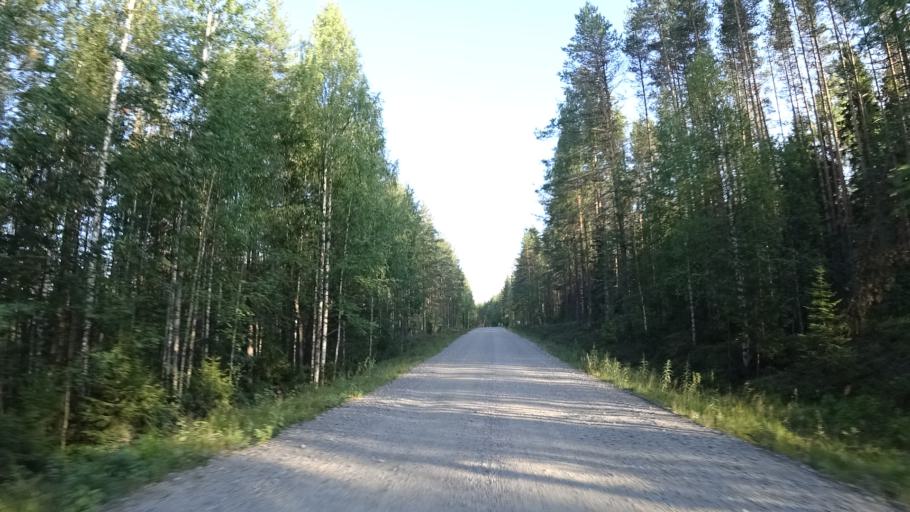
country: FI
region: North Karelia
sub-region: Joensuu
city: Ilomantsi
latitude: 63.1315
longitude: 30.7103
